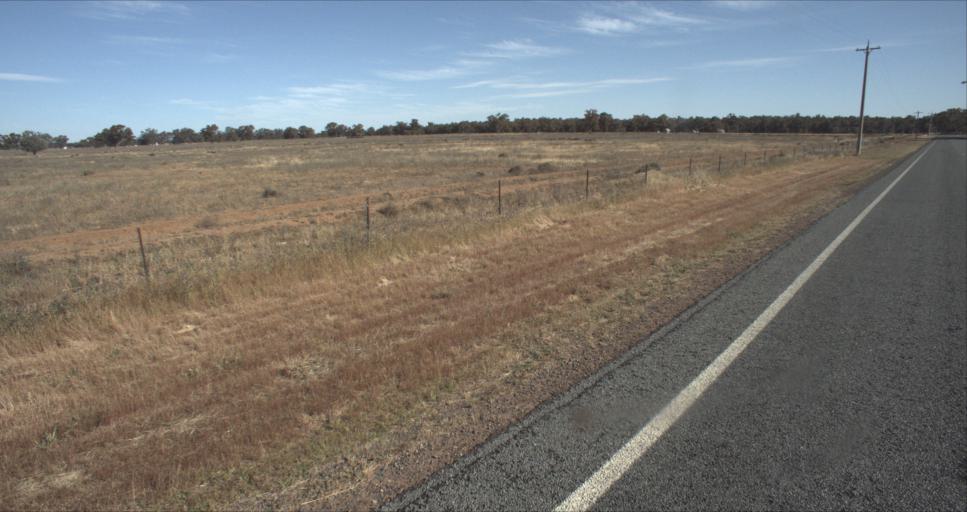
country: AU
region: New South Wales
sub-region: Leeton
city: Leeton
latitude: -34.6190
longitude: 146.3986
